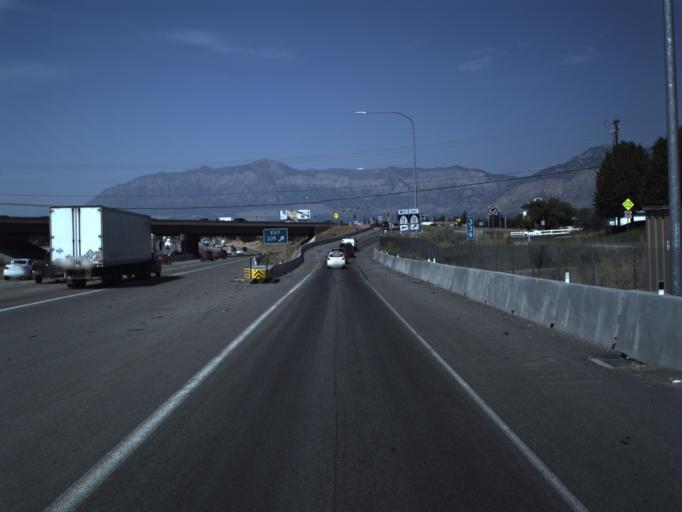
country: US
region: Utah
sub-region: Weber County
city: Roy
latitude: 41.1688
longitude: -112.0202
